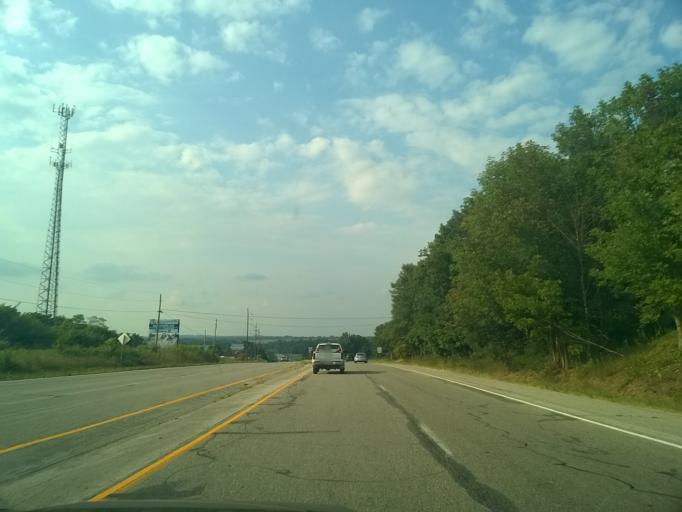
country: US
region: Indiana
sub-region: Putnam County
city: Cloverdale
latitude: 39.5377
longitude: -86.8037
